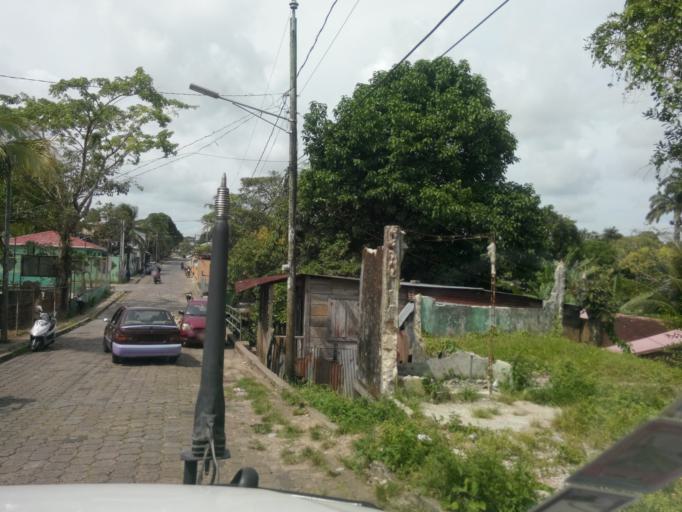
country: NI
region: Atlantico Sur
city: Bluefields
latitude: 12.0107
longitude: -83.7677
